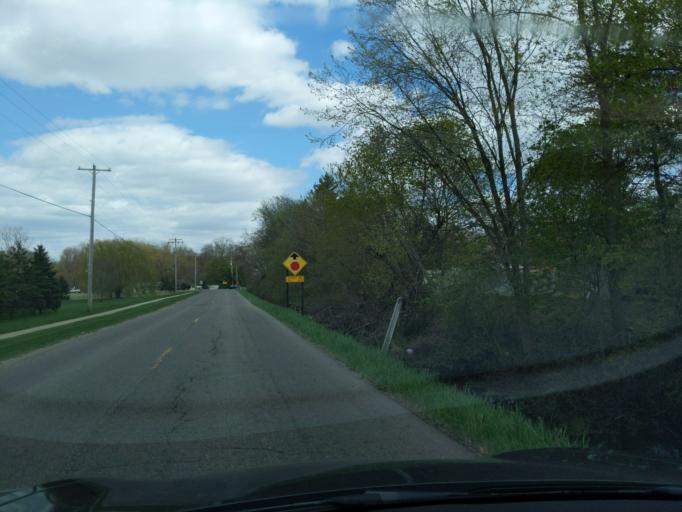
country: US
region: Michigan
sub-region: Ingham County
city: Holt
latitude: 42.6259
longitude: -84.5453
